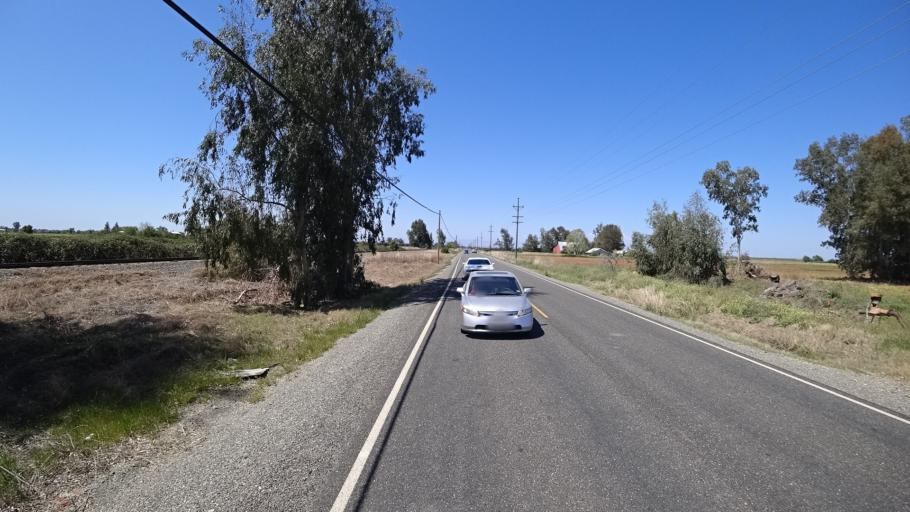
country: US
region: California
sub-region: Glenn County
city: Orland
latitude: 39.7685
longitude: -122.1161
